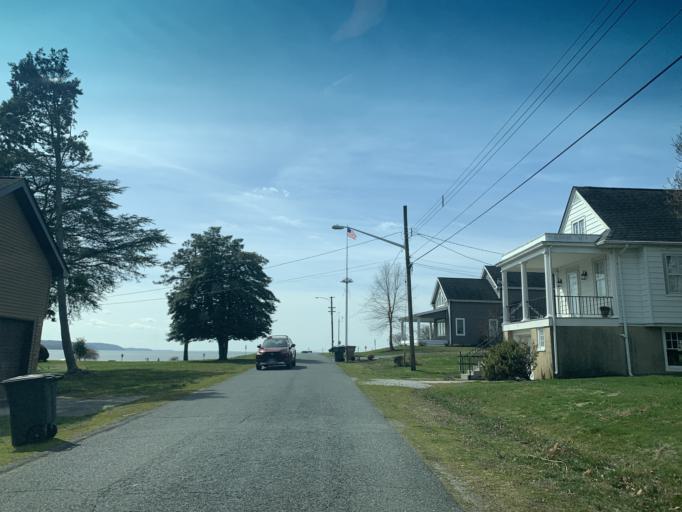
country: US
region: Maryland
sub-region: Cecil County
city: Charlestown
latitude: 39.5714
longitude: -75.9730
